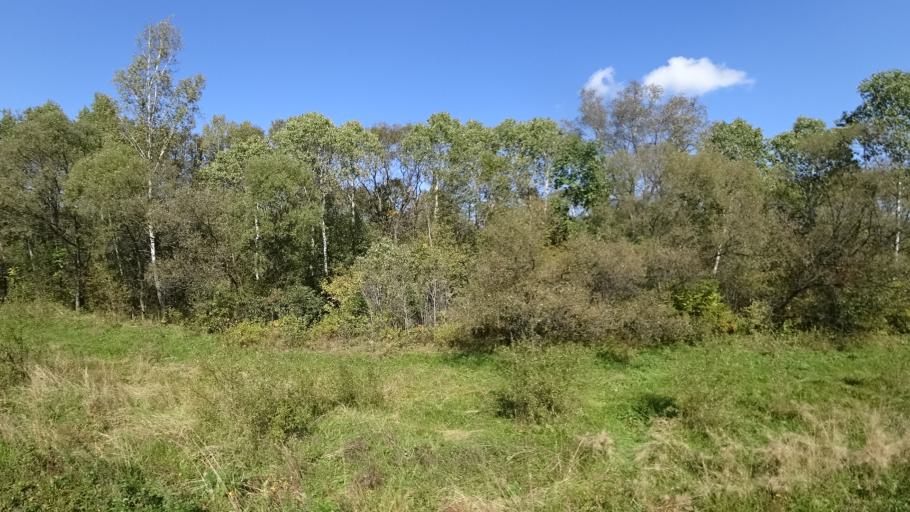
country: RU
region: Amur
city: Arkhara
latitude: 49.4055
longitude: 130.1267
